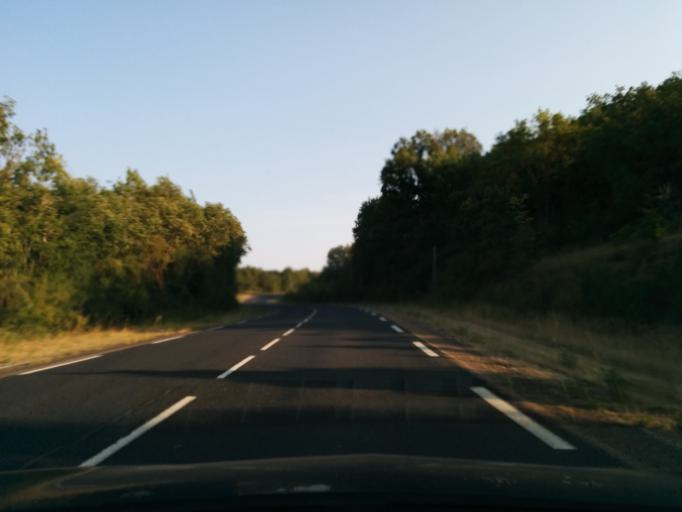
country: FR
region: Midi-Pyrenees
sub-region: Departement du Lot
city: Le Vigan
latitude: 44.6355
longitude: 1.4863
